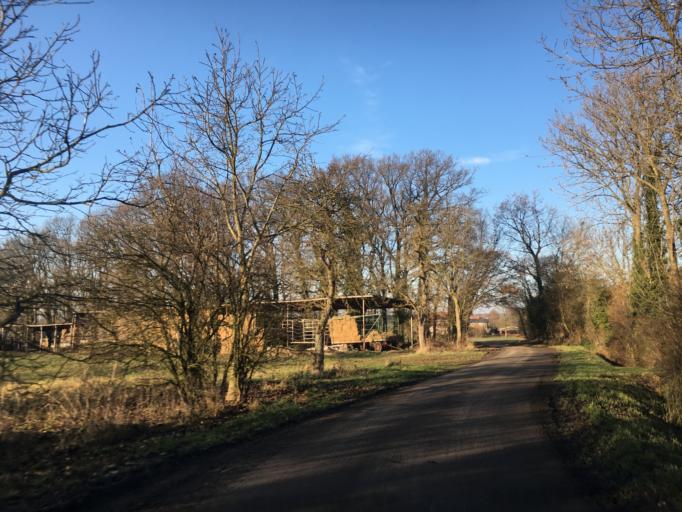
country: DE
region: North Rhine-Westphalia
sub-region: Regierungsbezirk Munster
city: Altenberge
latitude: 52.0275
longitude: 7.5430
